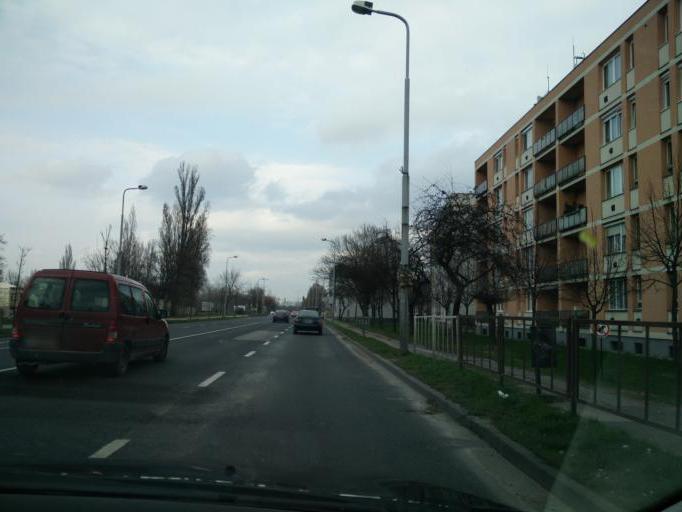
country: HU
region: Gyor-Moson-Sopron
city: Gyor
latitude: 47.6944
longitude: 17.6573
